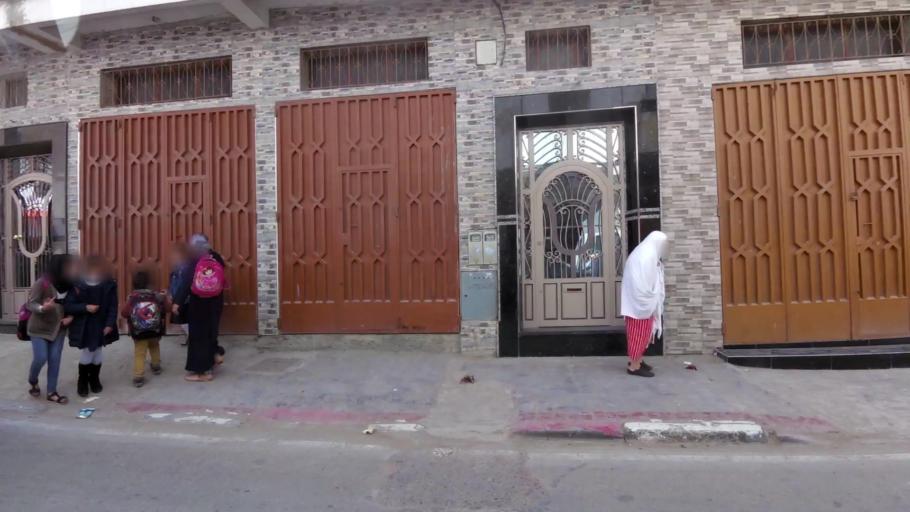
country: MA
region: Tanger-Tetouan
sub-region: Tanger-Assilah
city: Tangier
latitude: 35.7405
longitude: -5.8272
